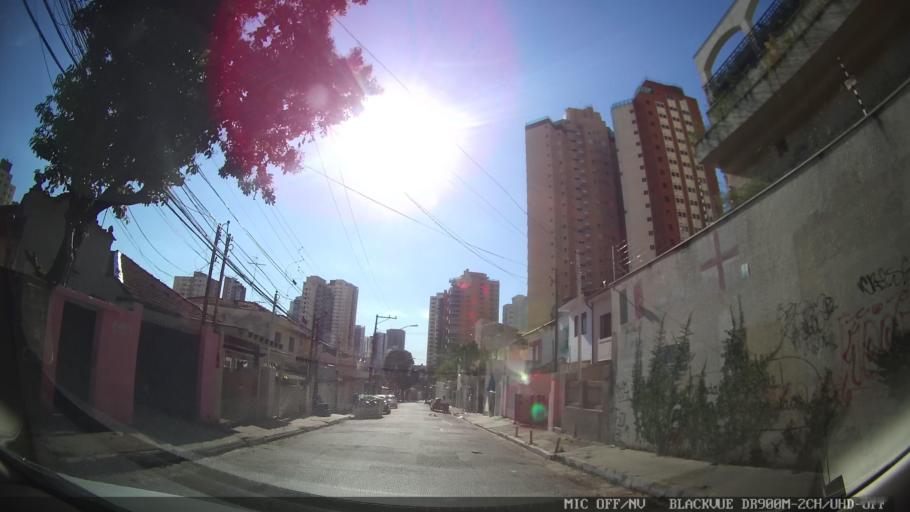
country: BR
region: Sao Paulo
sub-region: Sao Paulo
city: Sao Paulo
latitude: -23.4940
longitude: -46.6289
